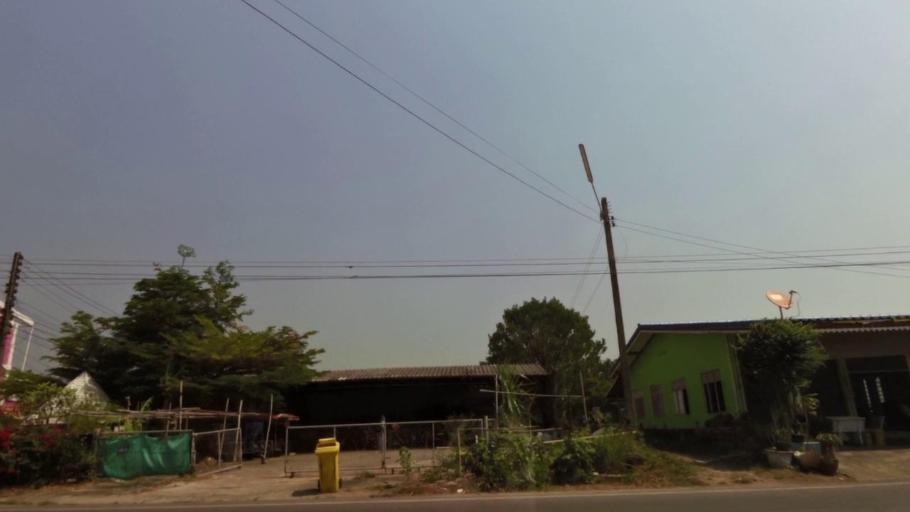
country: TH
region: Chanthaburi
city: Tha Mai
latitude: 12.5418
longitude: 101.9512
